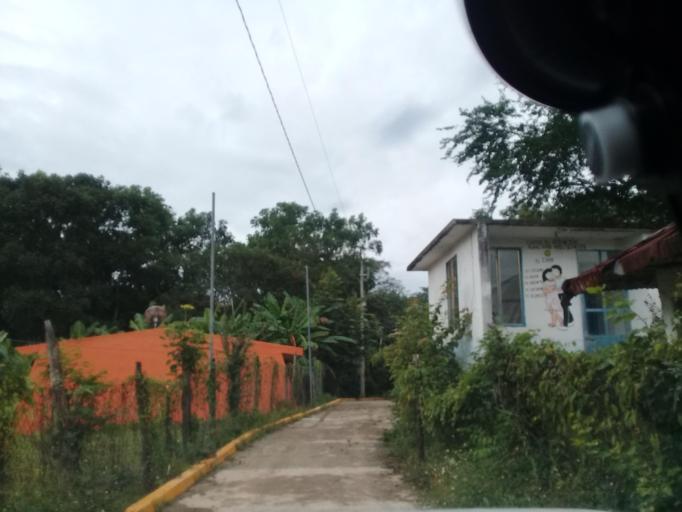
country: MX
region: Hidalgo
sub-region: Huejutla de Reyes
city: Chalahuiyapa
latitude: 21.1972
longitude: -98.3328
